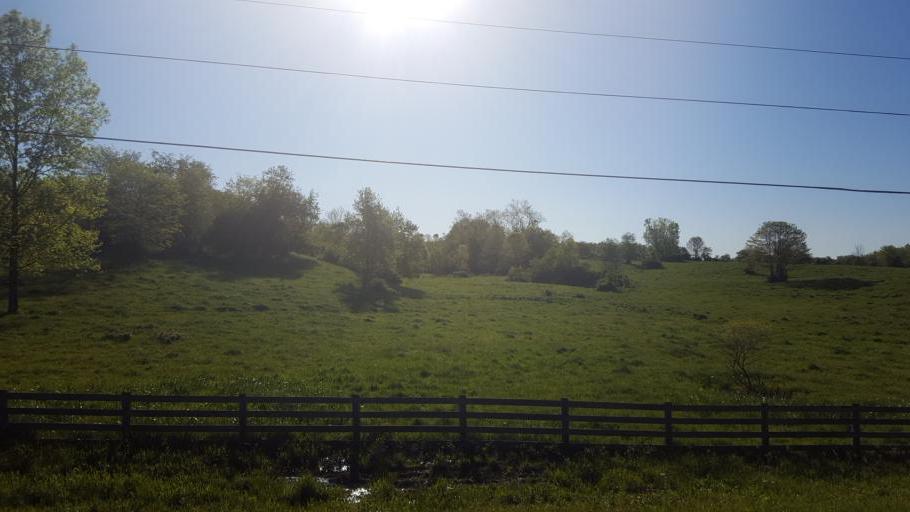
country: US
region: Ohio
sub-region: Delaware County
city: Sunbury
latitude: 40.2009
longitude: -82.8718
